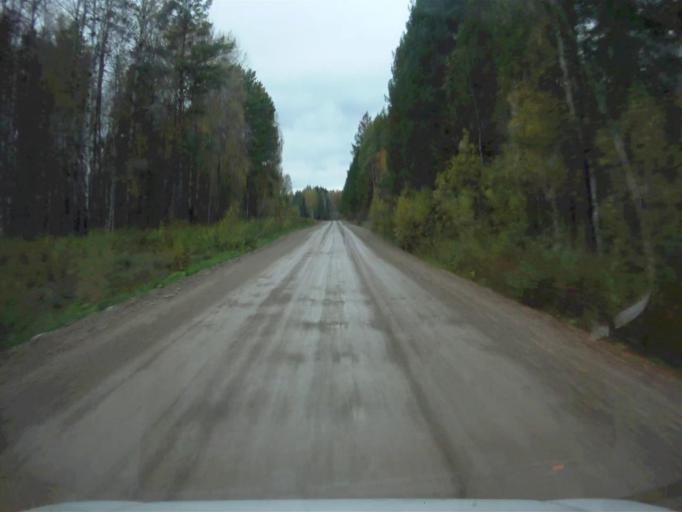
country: RU
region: Chelyabinsk
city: Nyazepetrovsk
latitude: 56.0949
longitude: 59.4030
